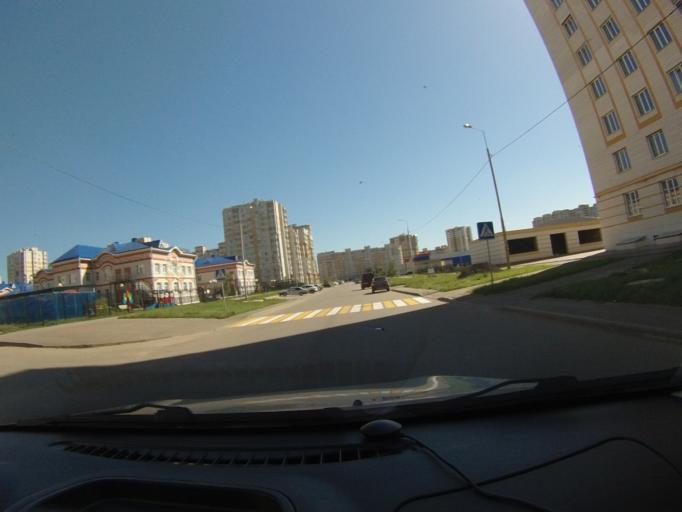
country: RU
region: Tambov
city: Tambov
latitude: 52.7690
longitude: 41.3965
